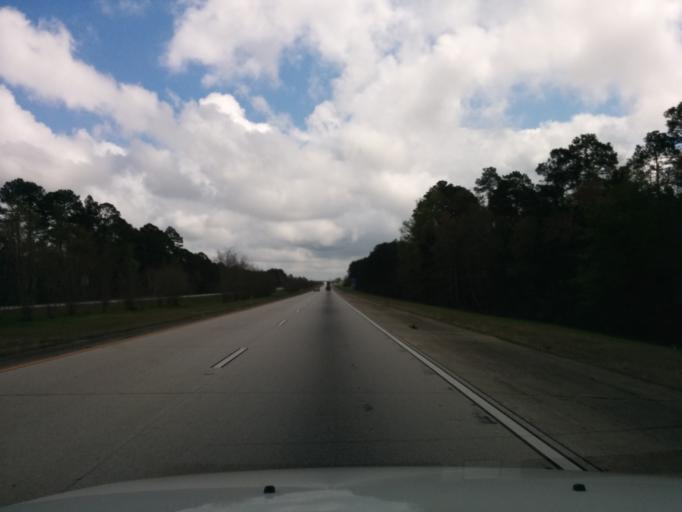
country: US
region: Georgia
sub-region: Evans County
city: Claxton
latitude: 32.3104
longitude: -81.8892
